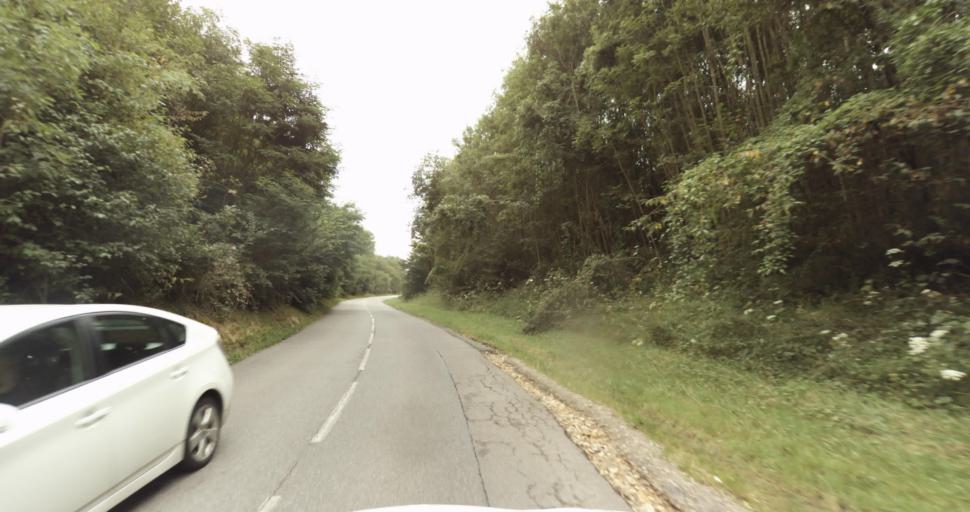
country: FR
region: Haute-Normandie
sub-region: Departement de l'Eure
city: Gravigny
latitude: 49.0427
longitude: 1.1724
